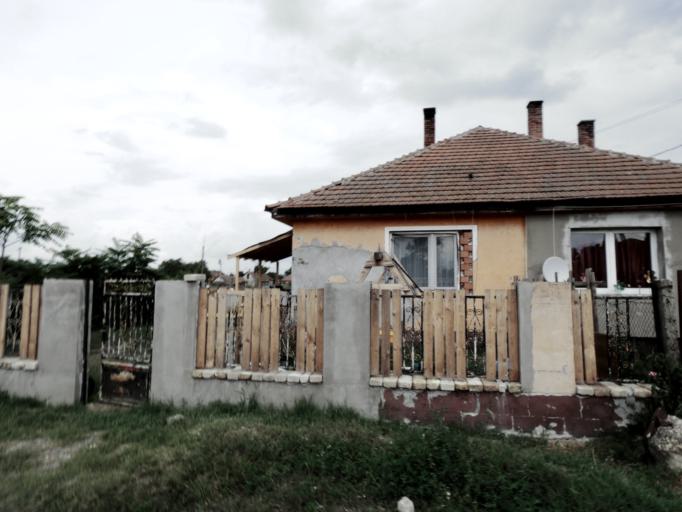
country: HU
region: Pest
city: Orkeny
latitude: 47.1313
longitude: 19.4486
